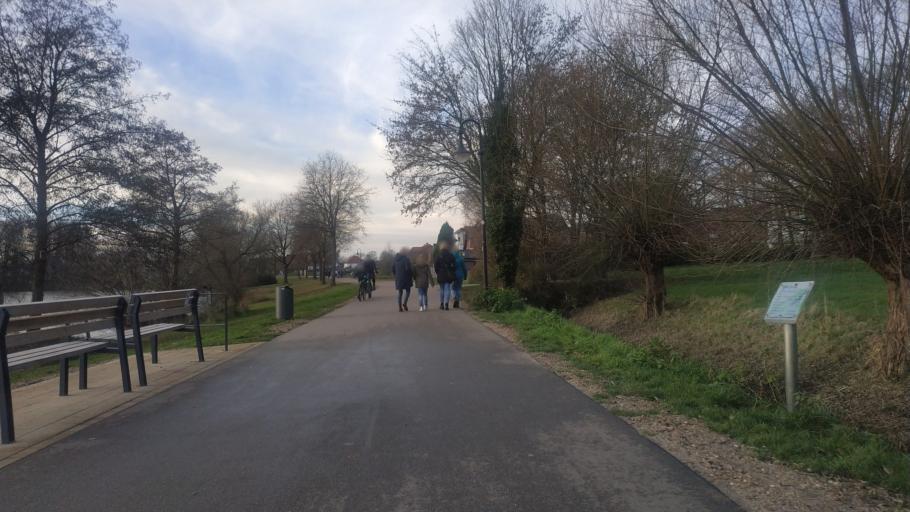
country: DE
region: North Rhine-Westphalia
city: Ibbenburen
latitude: 52.2683
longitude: 7.7268
